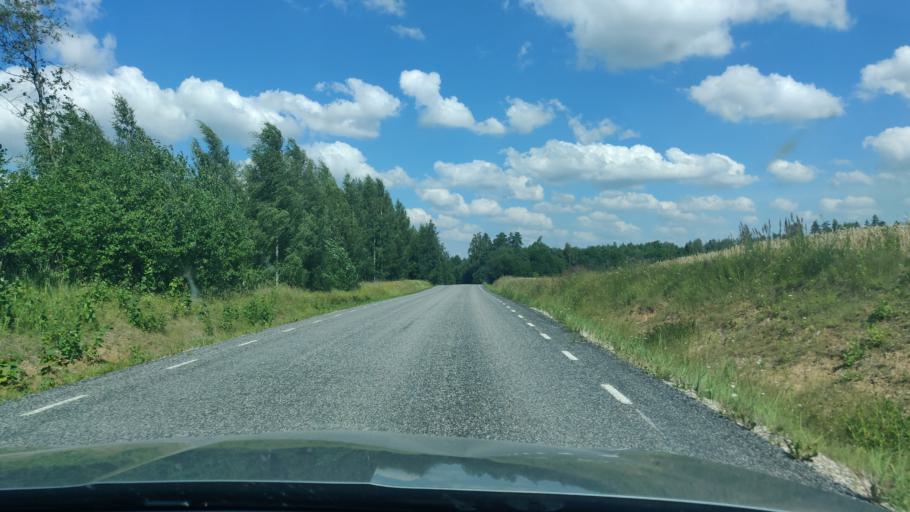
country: EE
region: Tartu
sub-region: Elva linn
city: Elva
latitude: 58.1485
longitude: 26.4738
